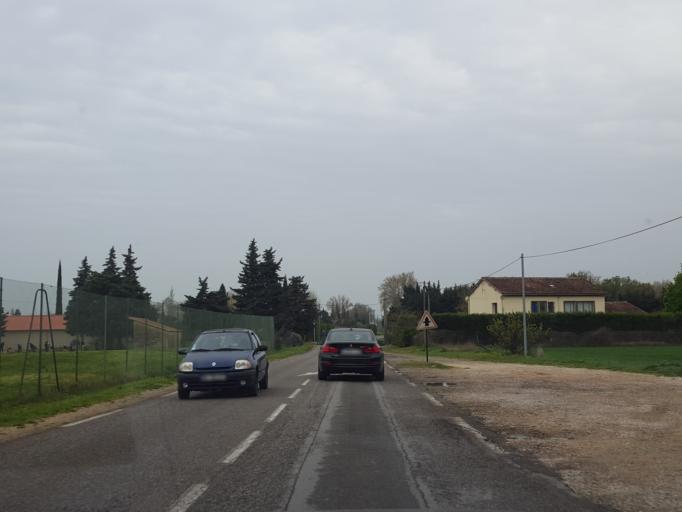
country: FR
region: Provence-Alpes-Cote d'Azur
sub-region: Departement du Vaucluse
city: Morieres-les-Avignon
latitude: 43.9253
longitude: 4.9014
